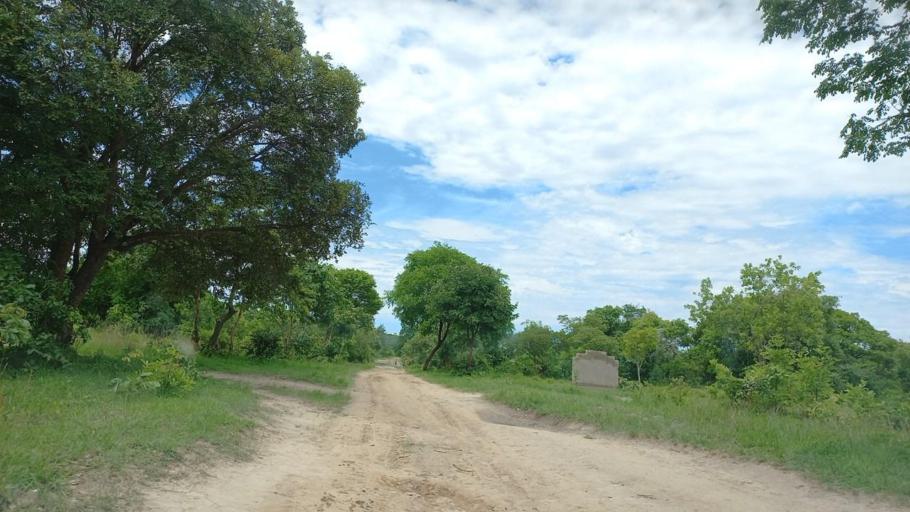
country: ZM
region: North-Western
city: Kabompo
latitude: -13.6182
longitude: 24.2135
